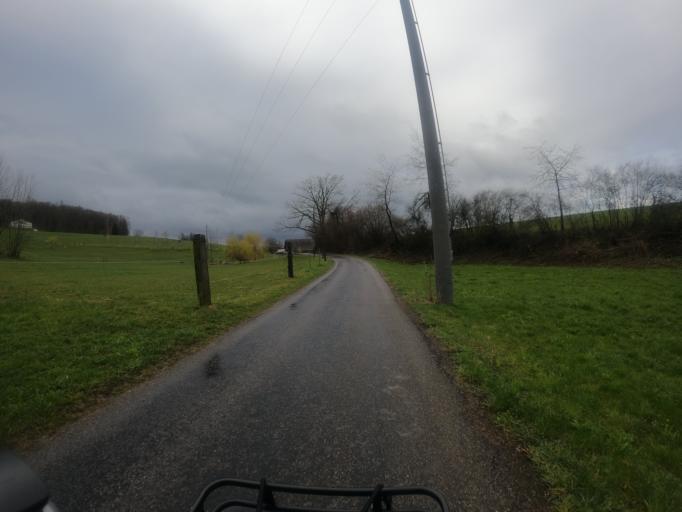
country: CH
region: Zurich
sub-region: Bezirk Affoltern
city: Mettmenstetten
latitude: 47.2581
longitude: 8.4615
